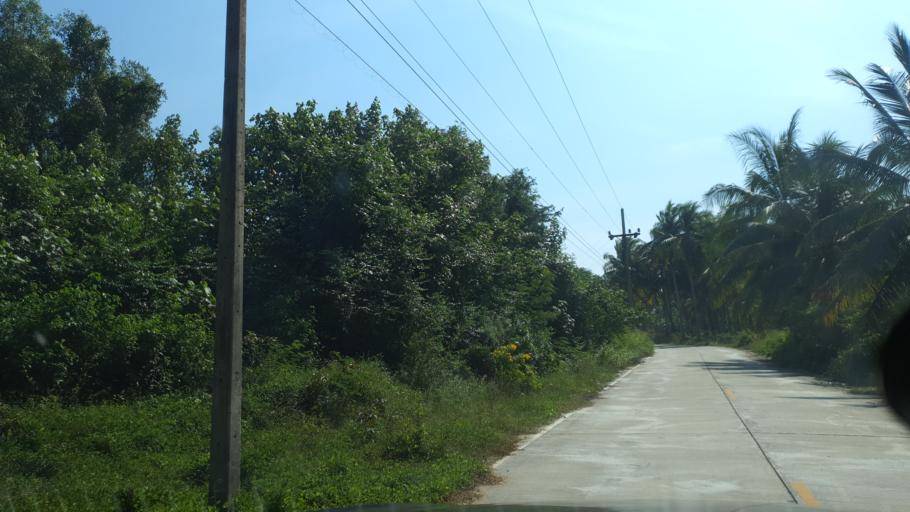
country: TH
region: Surat Thani
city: Tha Chana
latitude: 9.5982
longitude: 99.2056
